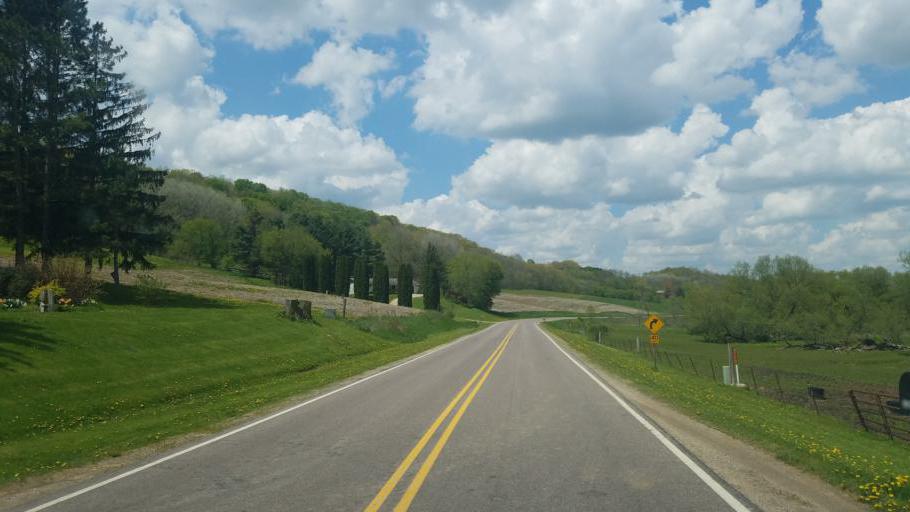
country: US
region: Wisconsin
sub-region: Vernon County
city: Hillsboro
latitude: 43.6179
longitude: -90.3447
